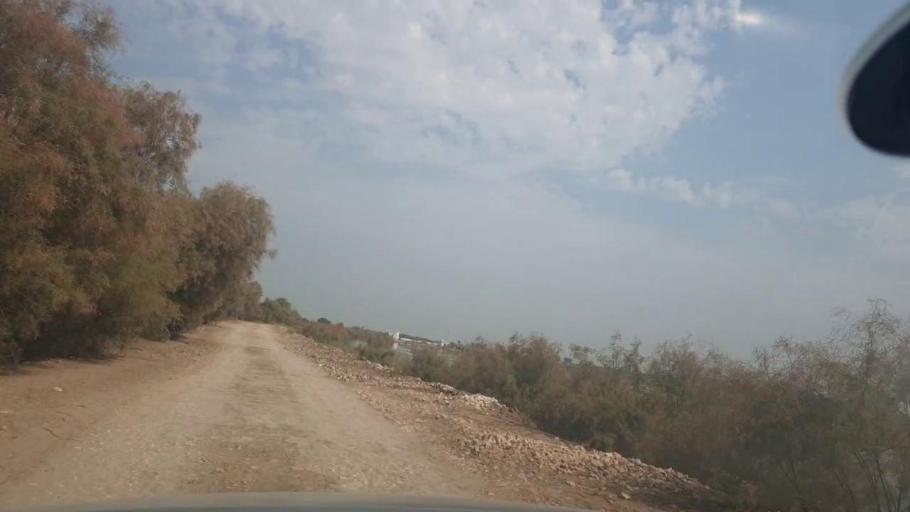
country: PK
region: Balochistan
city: Mehrabpur
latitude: 28.1084
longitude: 68.0907
